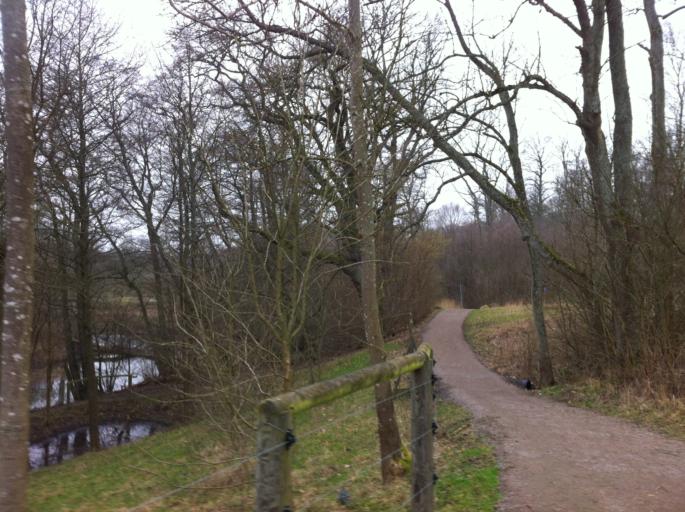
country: SE
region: Skane
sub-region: Helsingborg
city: Gantofta
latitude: 55.9991
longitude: 12.7891
